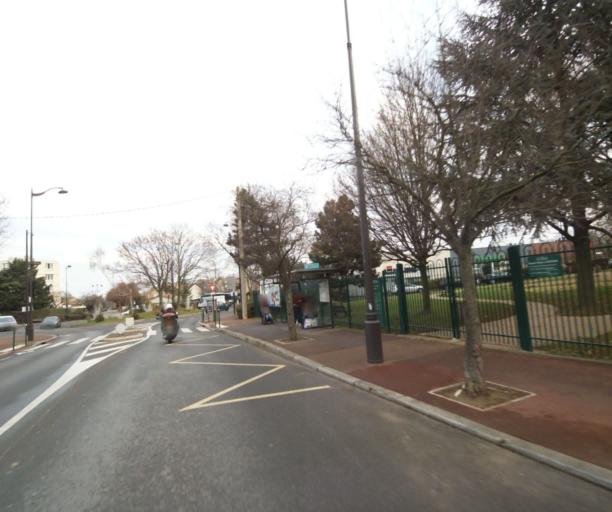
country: FR
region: Ile-de-France
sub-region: Departement des Hauts-de-Seine
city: Rueil-Malmaison
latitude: 48.8758
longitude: 2.2010
